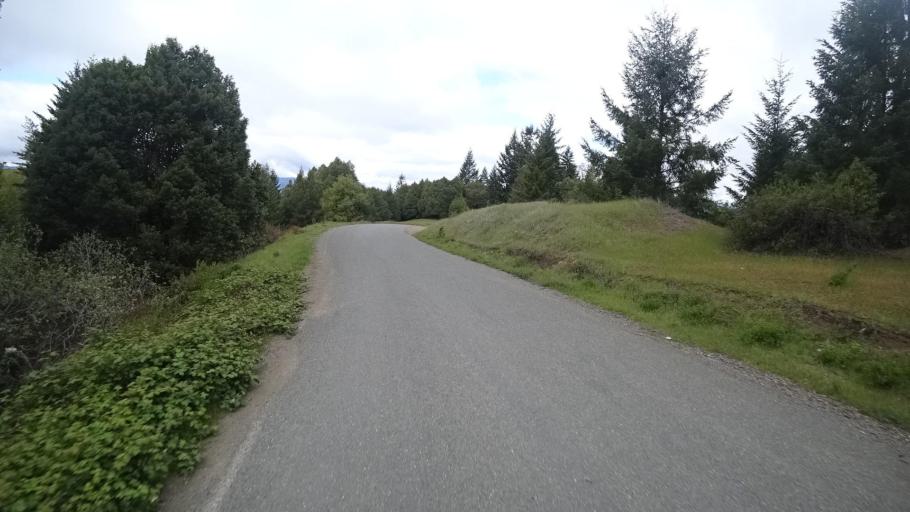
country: US
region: California
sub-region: Humboldt County
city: Redway
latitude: 40.1651
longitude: -123.5613
